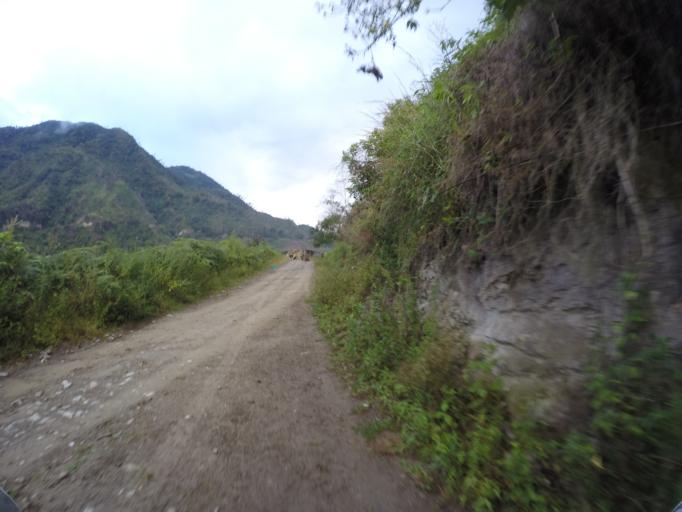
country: CO
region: Tolima
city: Cajamarca
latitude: 4.5055
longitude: -75.3984
